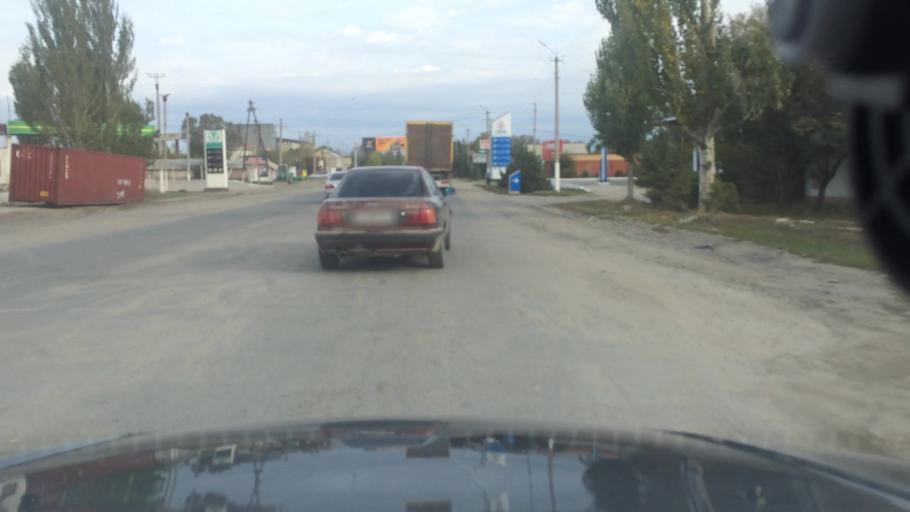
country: KG
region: Ysyk-Koel
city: Karakol
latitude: 42.5121
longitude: 78.3857
